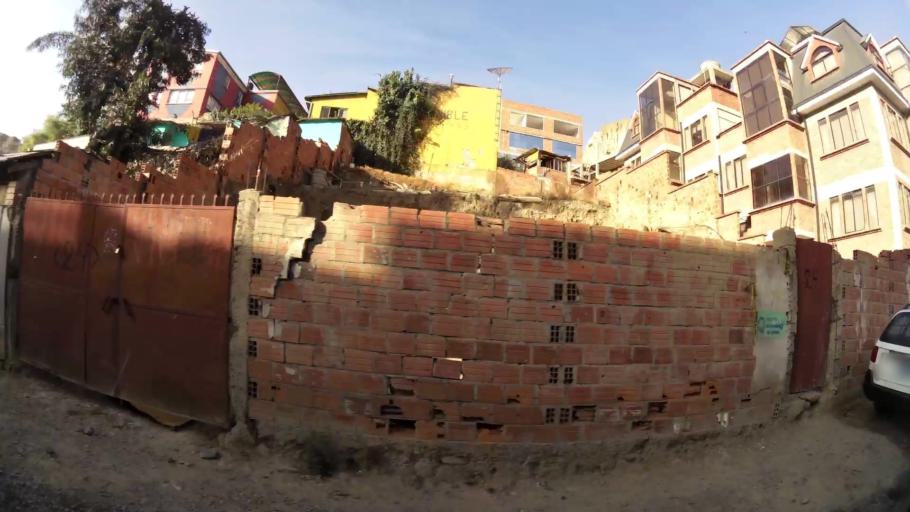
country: BO
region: La Paz
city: La Paz
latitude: -16.5257
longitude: -68.0996
